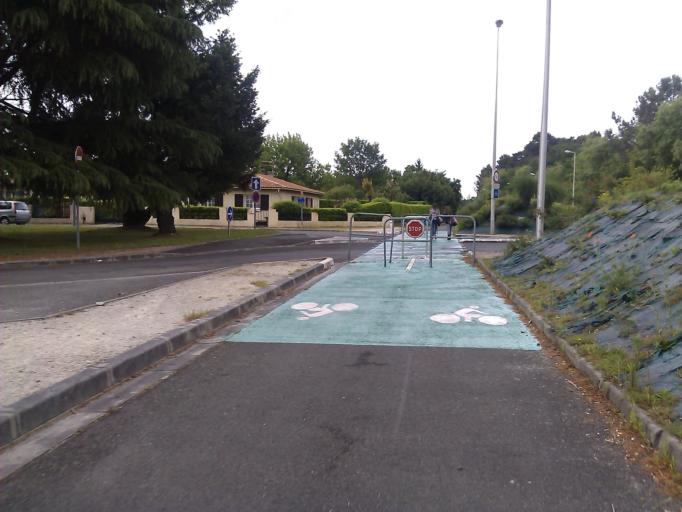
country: FR
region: Aquitaine
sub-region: Departement de la Gironde
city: Cestas
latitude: 44.7496
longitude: -0.6850
